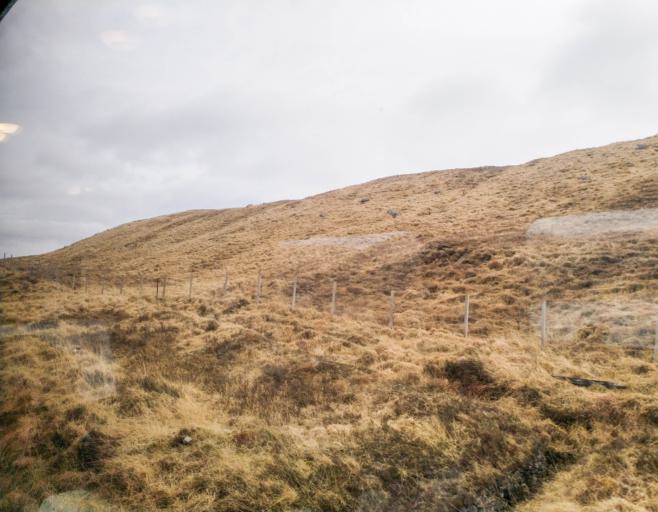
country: GB
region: Scotland
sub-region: Highland
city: Spean Bridge
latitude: 56.5506
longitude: -4.7481
